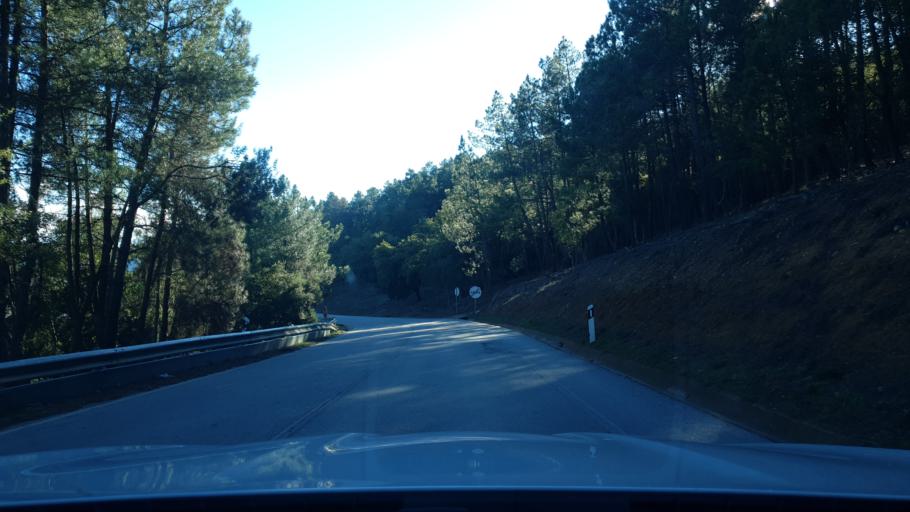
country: PT
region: Braganca
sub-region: Freixo de Espada A Cinta
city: Freixo de Espada a Cinta
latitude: 41.1050
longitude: -6.8283
